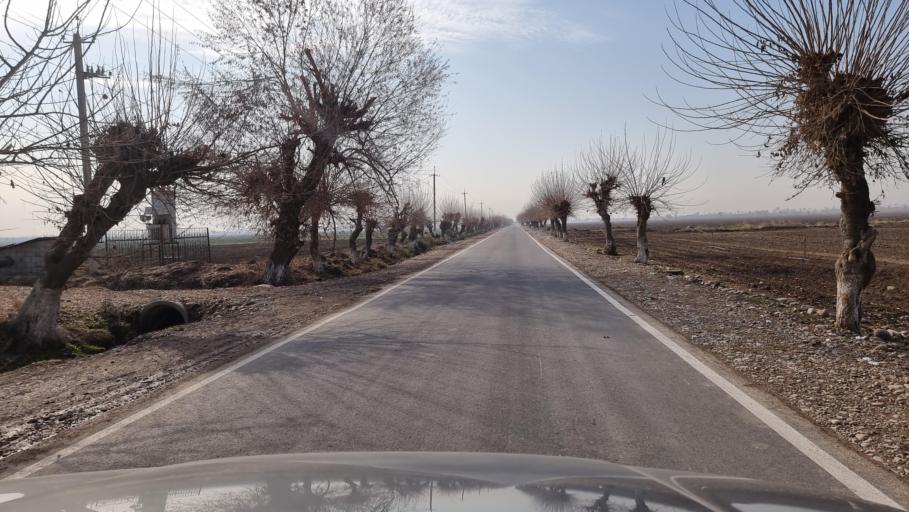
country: UZ
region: Toshkent
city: Tuytepa
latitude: 41.1011
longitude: 69.3830
